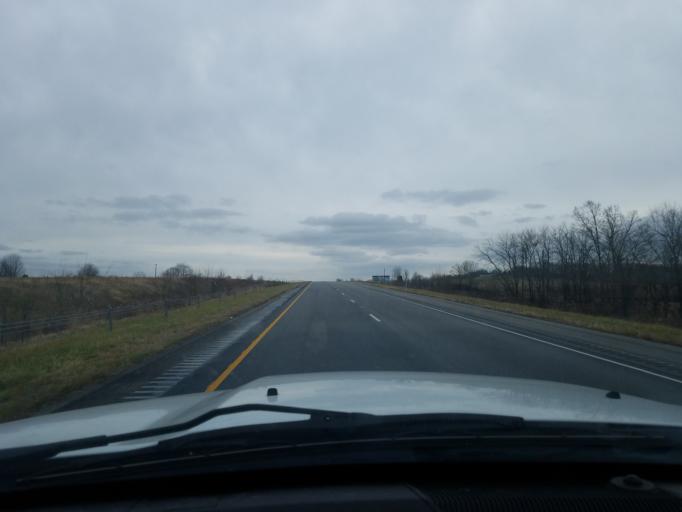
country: US
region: Indiana
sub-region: Dubois County
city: Ferdinand
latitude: 38.2328
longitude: -86.6691
